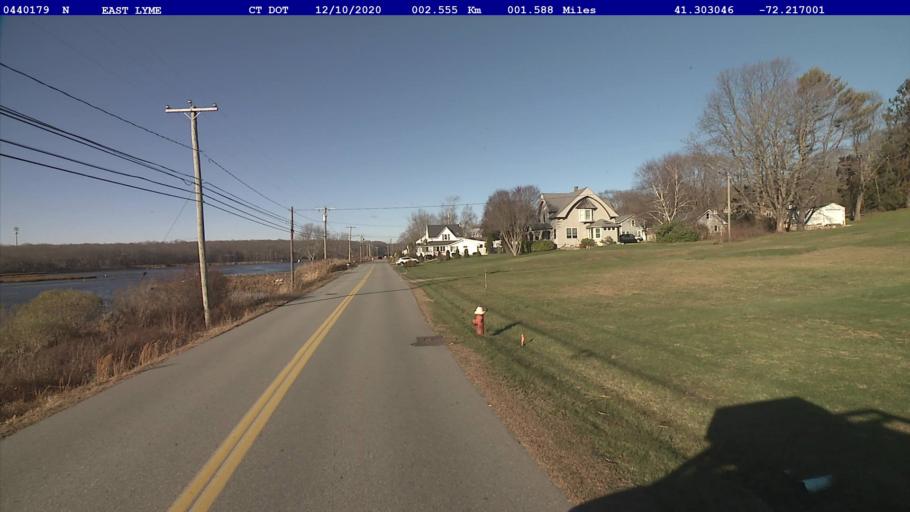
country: US
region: Connecticut
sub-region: New London County
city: Niantic
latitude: 41.3031
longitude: -72.2170
